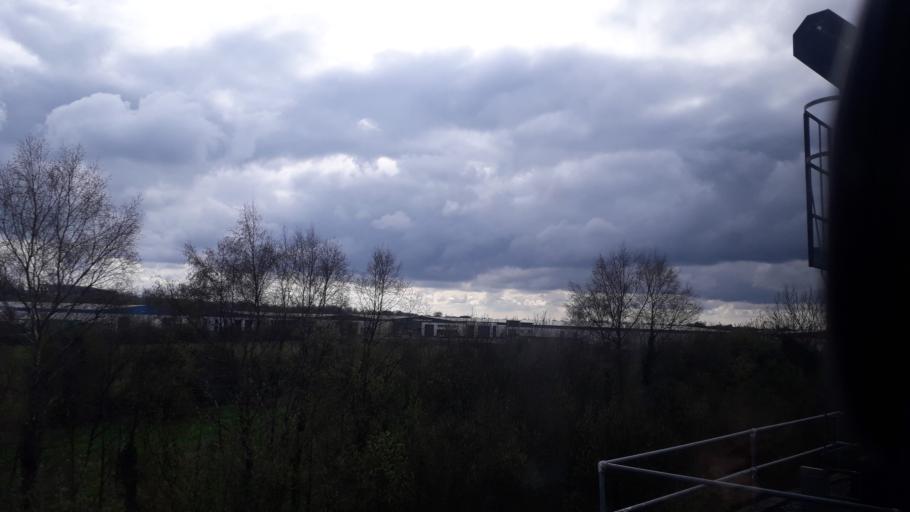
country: IE
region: Leinster
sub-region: An Longfort
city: Longford
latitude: 53.7227
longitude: -7.8033
